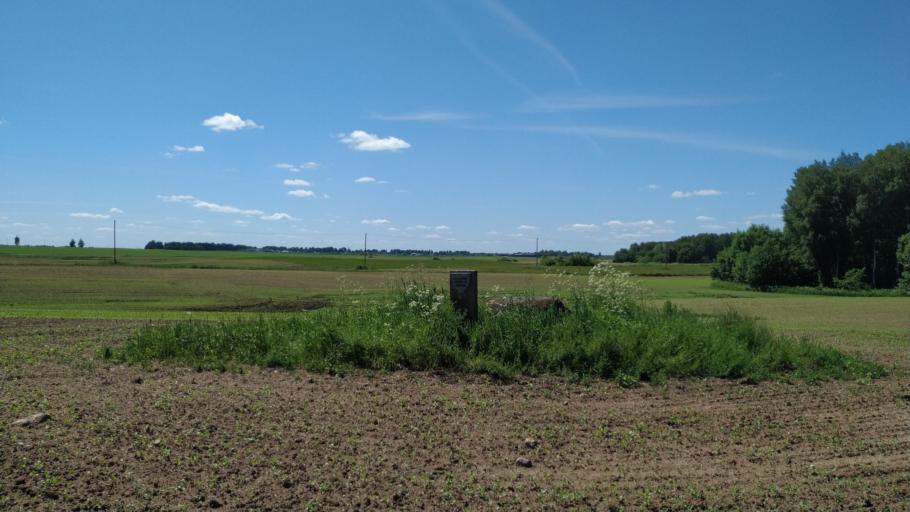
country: LT
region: Vilnius County
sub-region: Vilnius
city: Fabijoniskes
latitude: 55.0073
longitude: 25.2461
